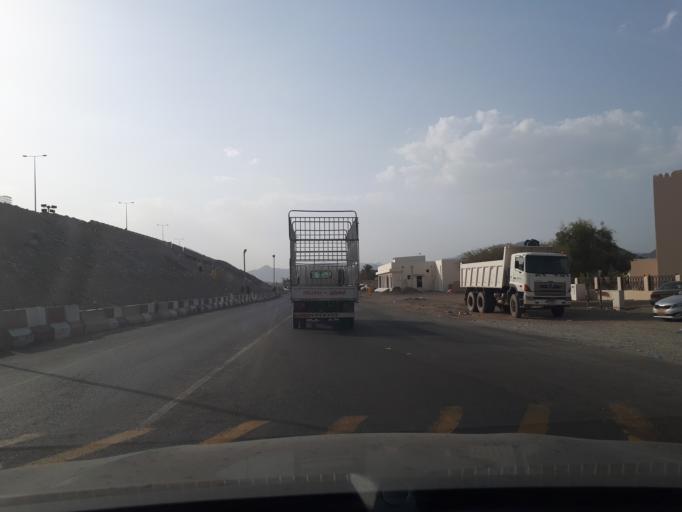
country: OM
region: Ash Sharqiyah
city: Ibra'
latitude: 22.8314
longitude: 58.4274
